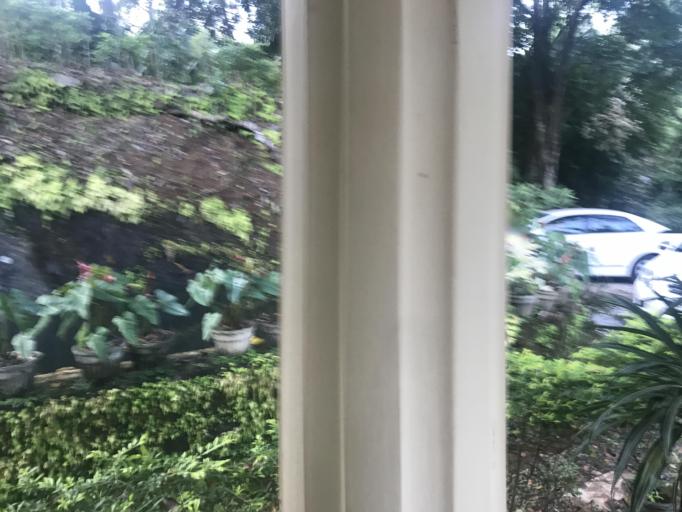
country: LK
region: Central
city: Kandy
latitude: 7.2469
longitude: 80.6148
